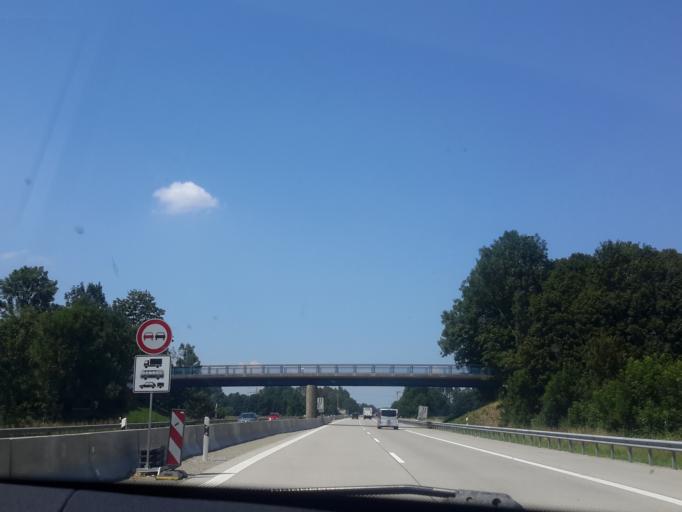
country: DE
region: Bavaria
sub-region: Upper Bavaria
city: Flintsbach
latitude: 47.7236
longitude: 12.1391
